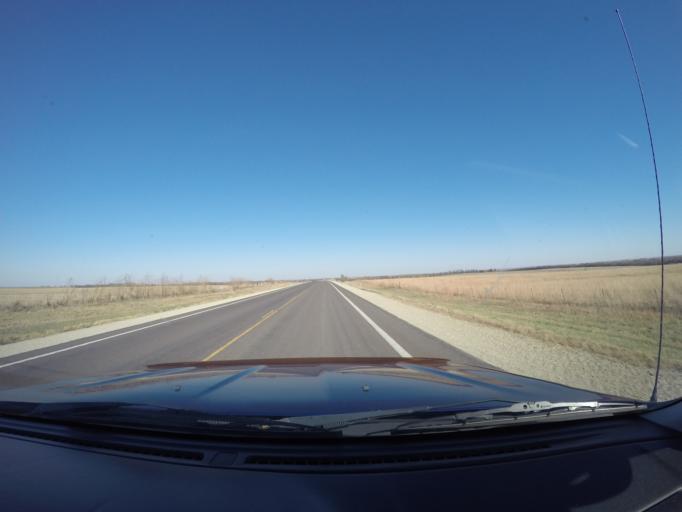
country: US
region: Kansas
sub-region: Marshall County
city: Blue Rapids
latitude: 39.6395
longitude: -96.7505
